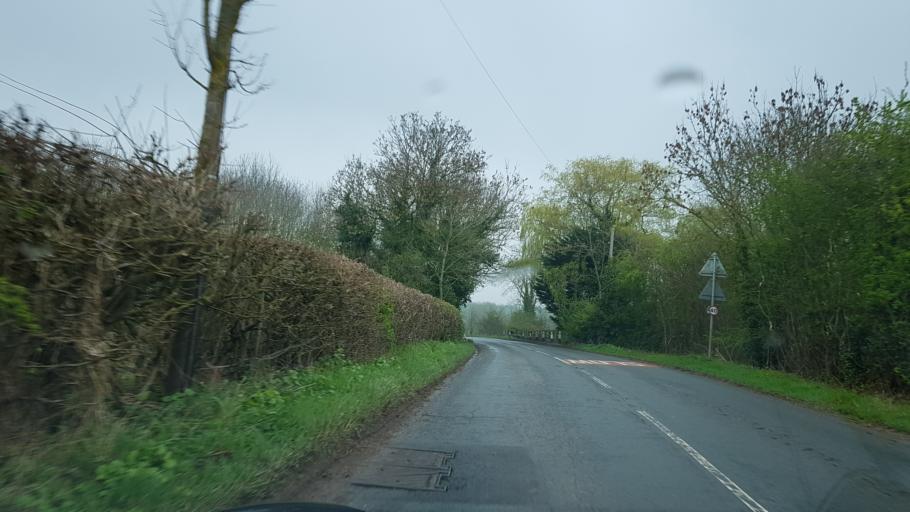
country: GB
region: England
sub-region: Herefordshire
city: Ledbury
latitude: 52.0719
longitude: -2.4521
